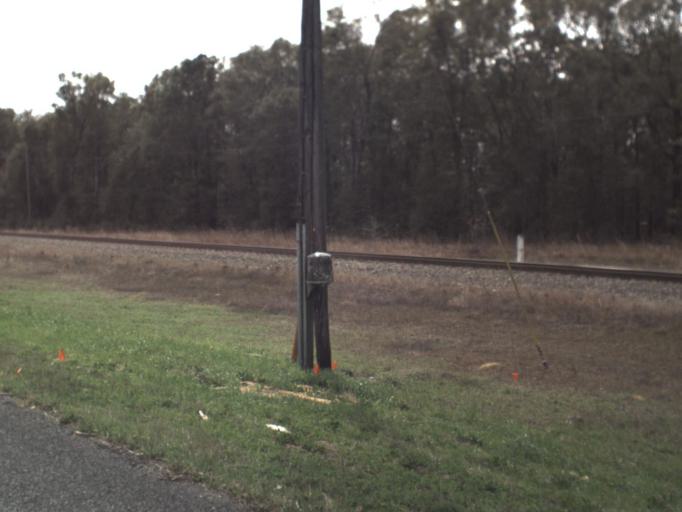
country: US
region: Florida
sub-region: Washington County
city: Chipley
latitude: 30.6364
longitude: -85.3994
